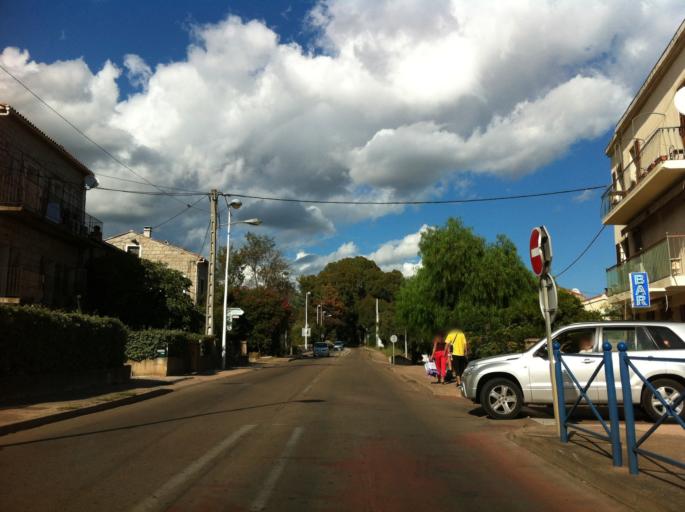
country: FR
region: Corsica
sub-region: Departement de la Corse-du-Sud
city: Porto-Vecchio
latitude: 41.6171
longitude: 9.2812
